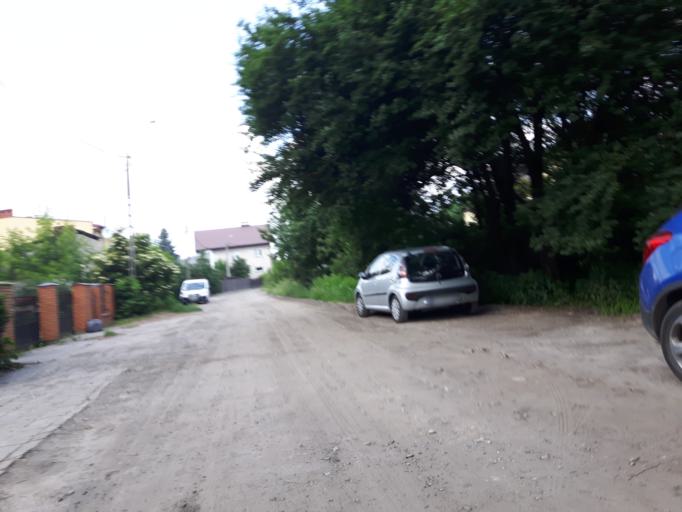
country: PL
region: Masovian Voivodeship
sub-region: Powiat wolominski
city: Zabki
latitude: 52.2827
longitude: 21.1166
